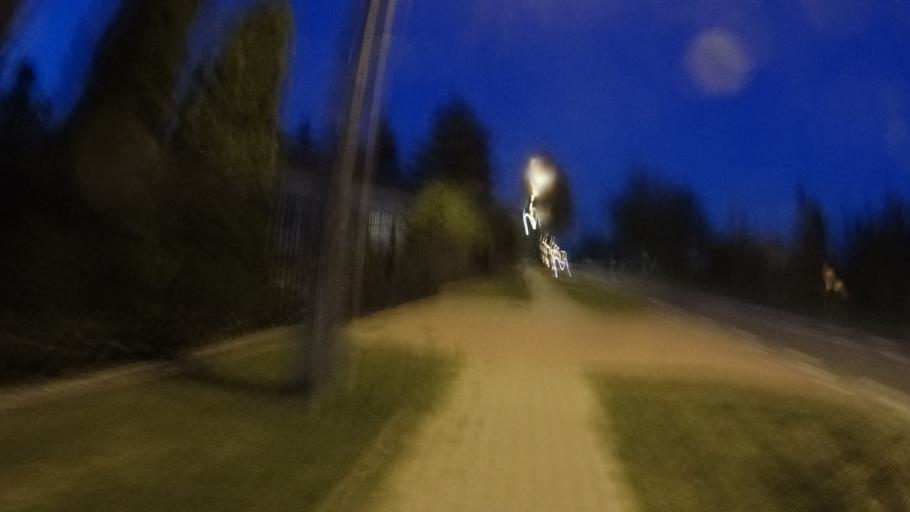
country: PL
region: Masovian Voivodeship
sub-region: Powiat warszawski zachodni
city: Jozefow
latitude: 52.2600
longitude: 20.6954
